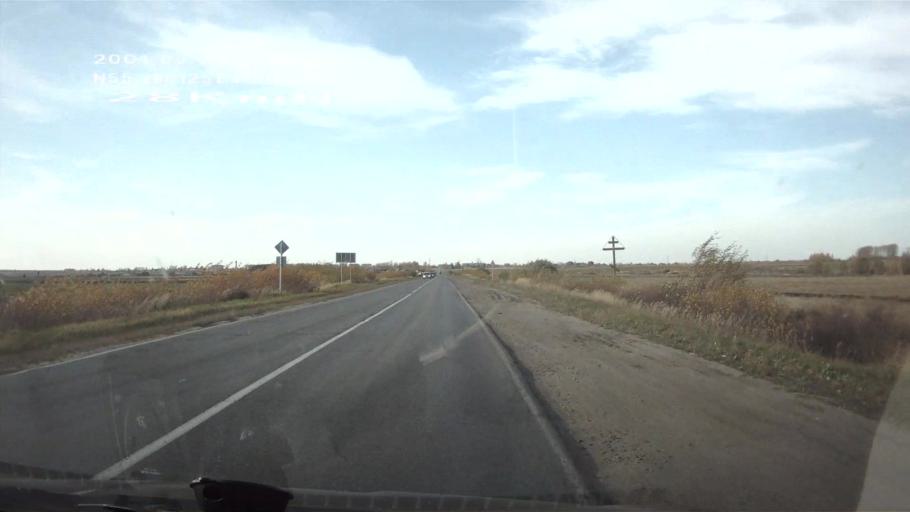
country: RU
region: Chuvashia
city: Ibresi
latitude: 55.2860
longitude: 47.0800
